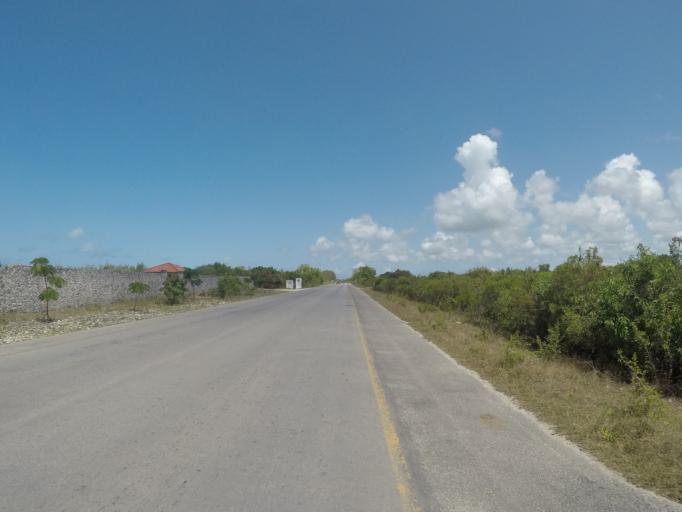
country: TZ
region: Zanzibar Central/South
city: Nganane
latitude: -6.3012
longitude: 39.5386
